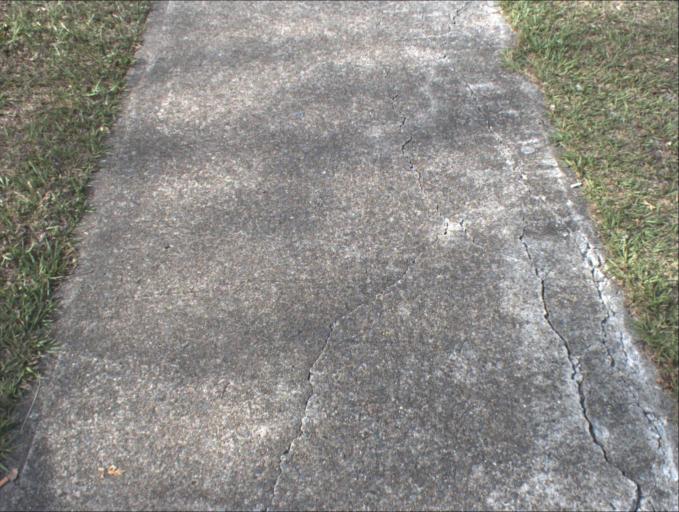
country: AU
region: Queensland
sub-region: Logan
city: Beenleigh
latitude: -27.7098
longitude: 153.2033
